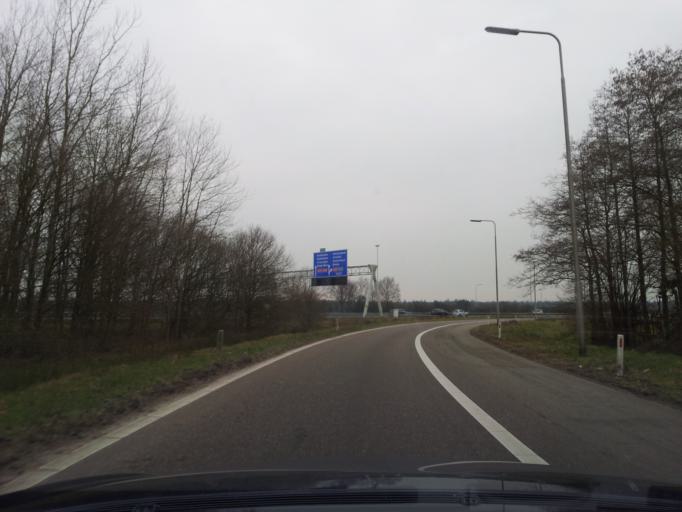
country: NL
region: North Brabant
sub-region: Gemeente Breda
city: Hoge Vucht
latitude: 51.5563
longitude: 4.8479
